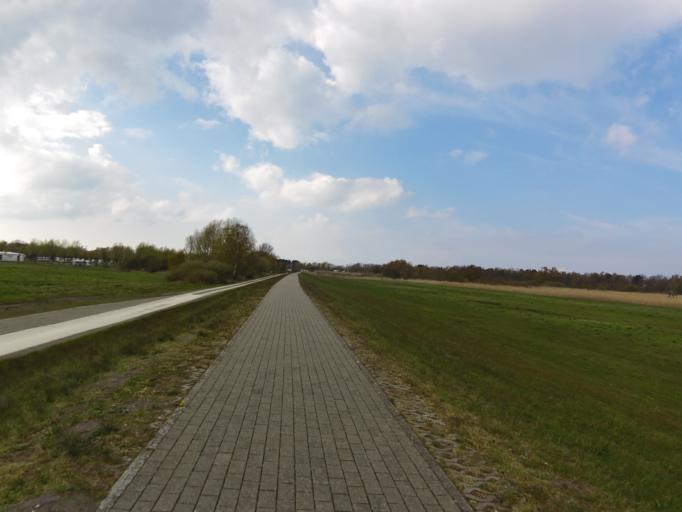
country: DE
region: Mecklenburg-Vorpommern
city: Zingst
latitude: 54.4367
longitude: 12.7124
